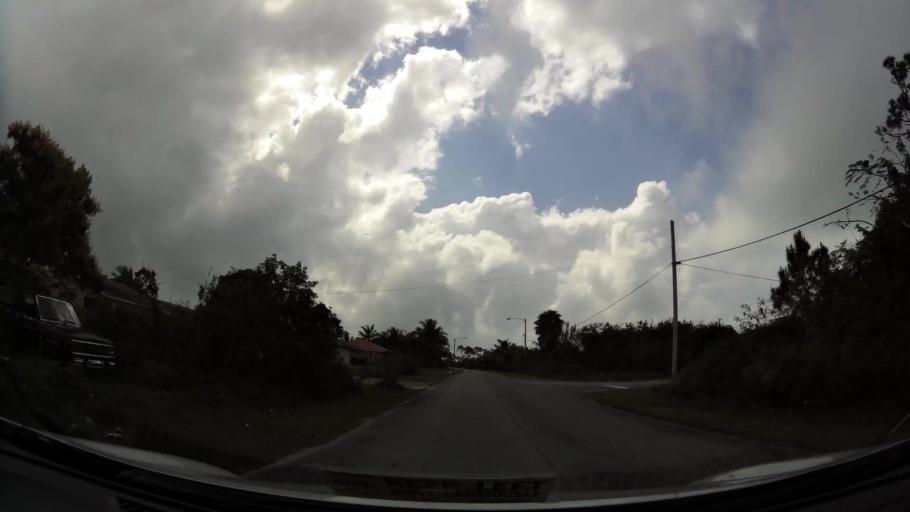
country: BS
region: Freeport
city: Lucaya
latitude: 26.5432
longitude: -78.5938
